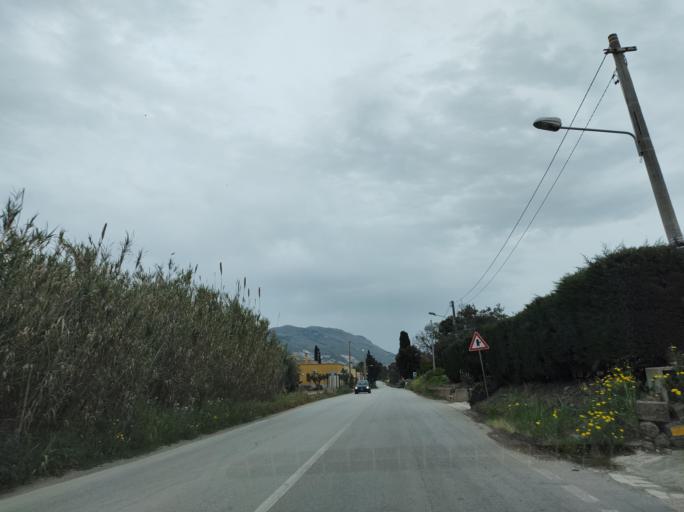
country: IT
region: Sicily
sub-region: Trapani
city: Custonaci
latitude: 38.0413
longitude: 12.6715
